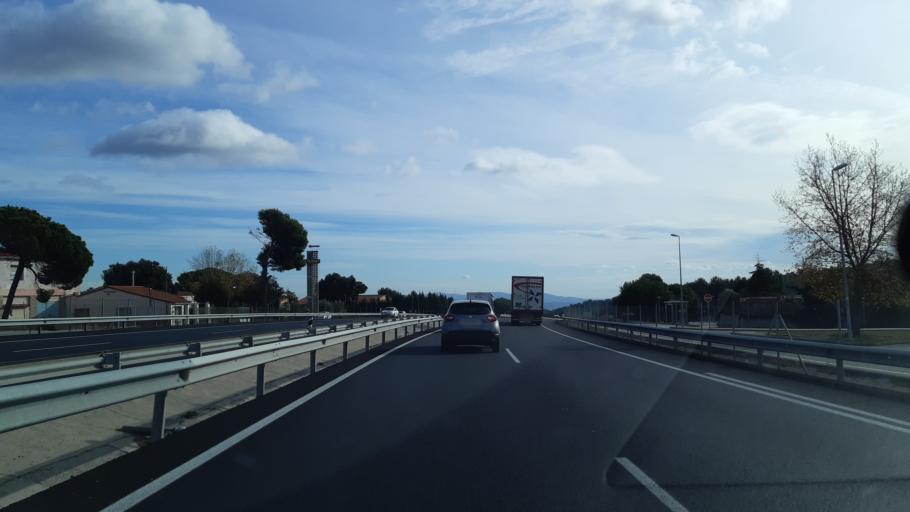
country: ES
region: Catalonia
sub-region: Provincia de Barcelona
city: Collbato
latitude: 41.5670
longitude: 1.8085
